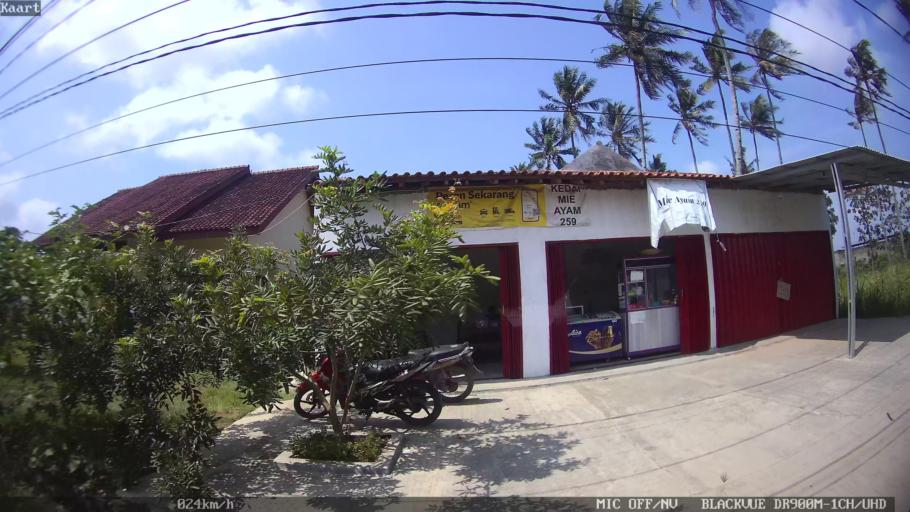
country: ID
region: Lampung
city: Kedaton
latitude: -5.3493
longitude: 105.2825
